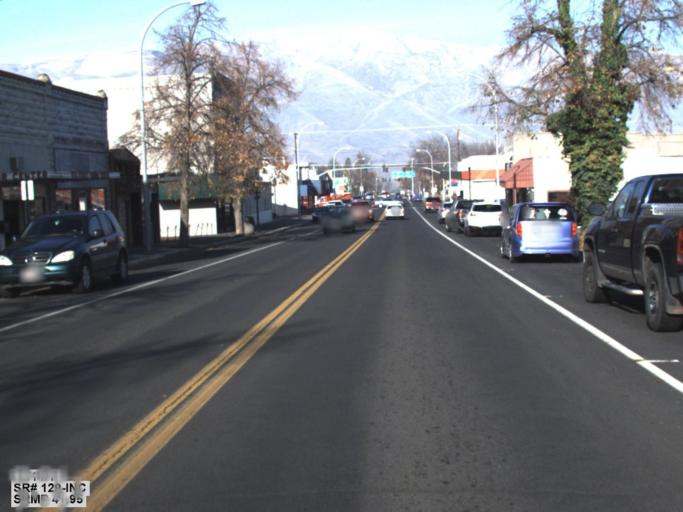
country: US
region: Washington
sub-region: Asotin County
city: Clarkston
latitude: 46.4130
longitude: -117.0456
